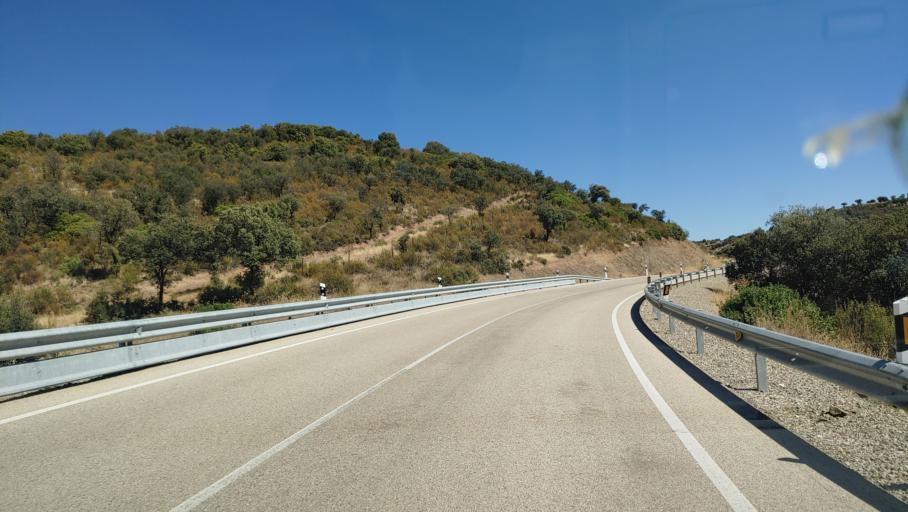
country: ES
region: Andalusia
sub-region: Provincia de Jaen
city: Genave
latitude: 38.4995
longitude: -2.7699
